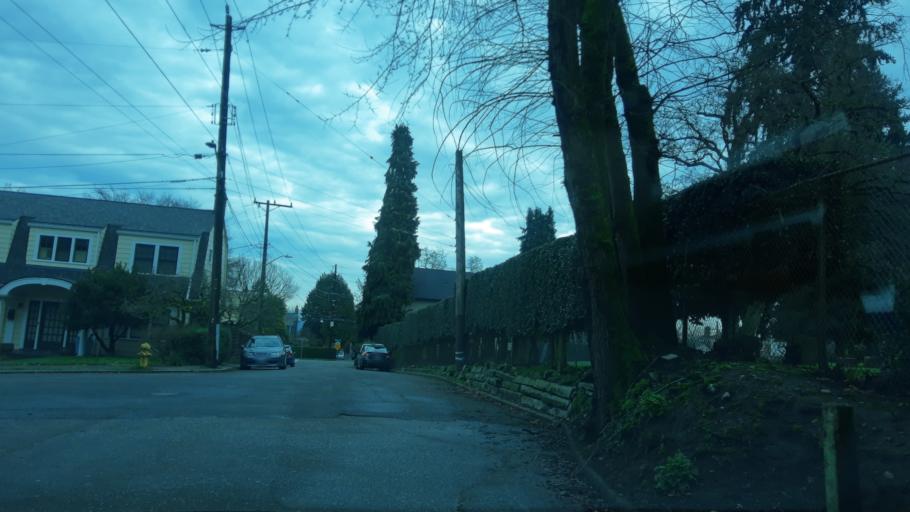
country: US
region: Washington
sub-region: King County
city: Seattle
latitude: 47.6360
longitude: -122.3151
